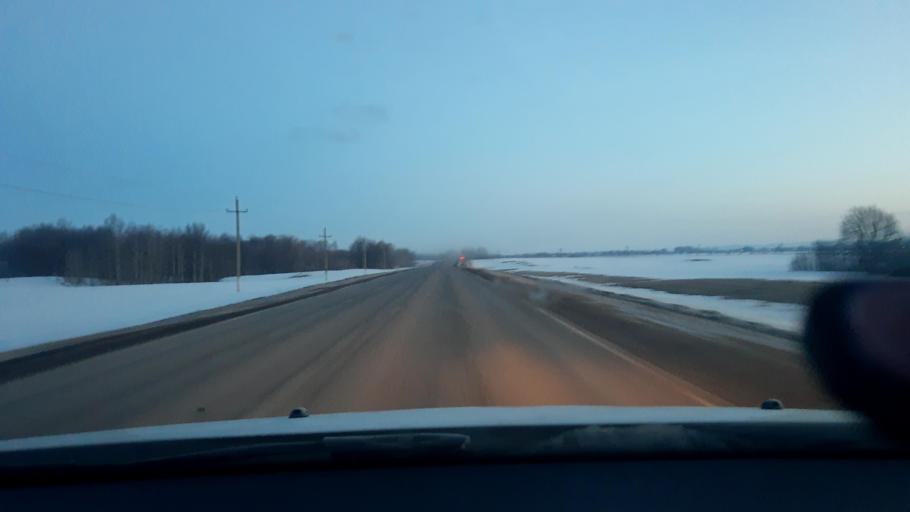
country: RU
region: Bashkortostan
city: Ulukulevo
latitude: 54.4140
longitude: 56.3691
